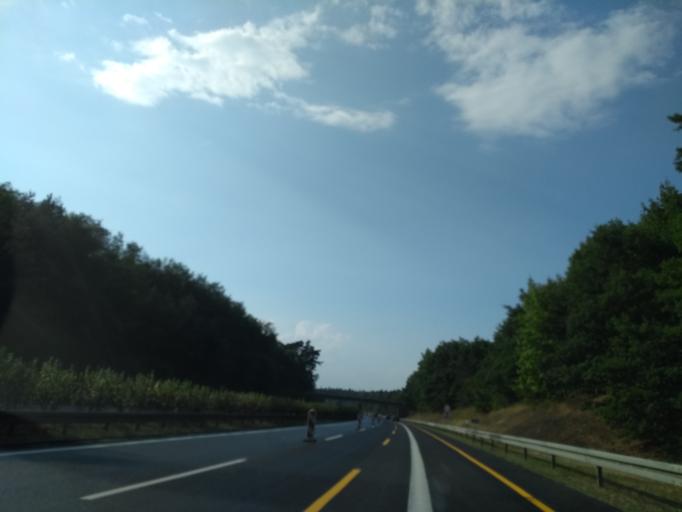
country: DE
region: Brandenburg
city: Bronkow
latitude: 51.6518
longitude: 13.9391
